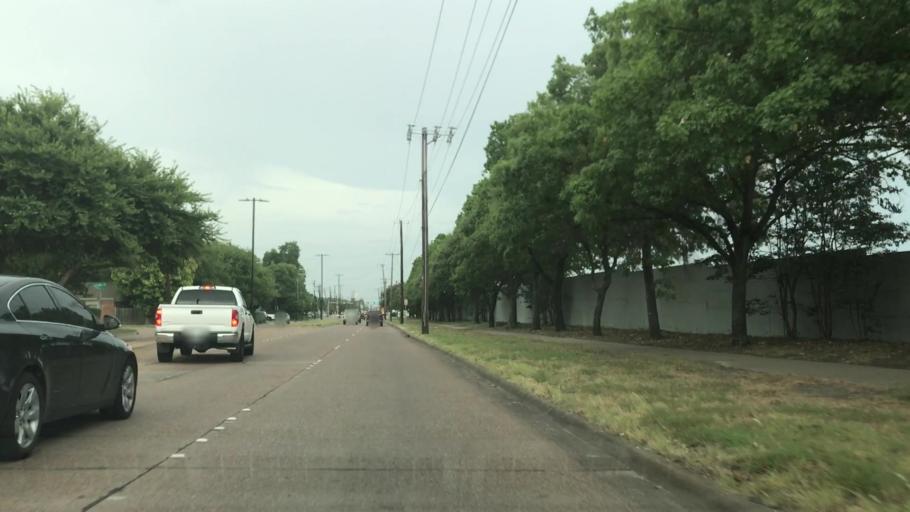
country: US
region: Texas
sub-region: Dallas County
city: Garland
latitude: 32.8788
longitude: -96.6644
